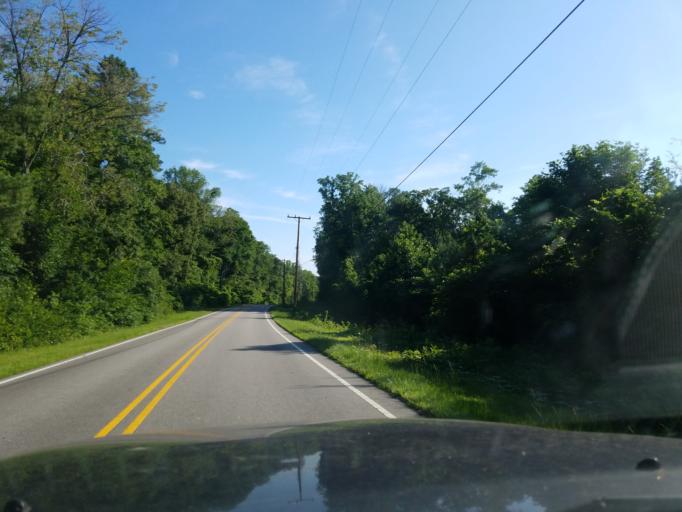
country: US
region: North Carolina
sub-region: Granville County
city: Butner
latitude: 36.1485
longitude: -78.7689
